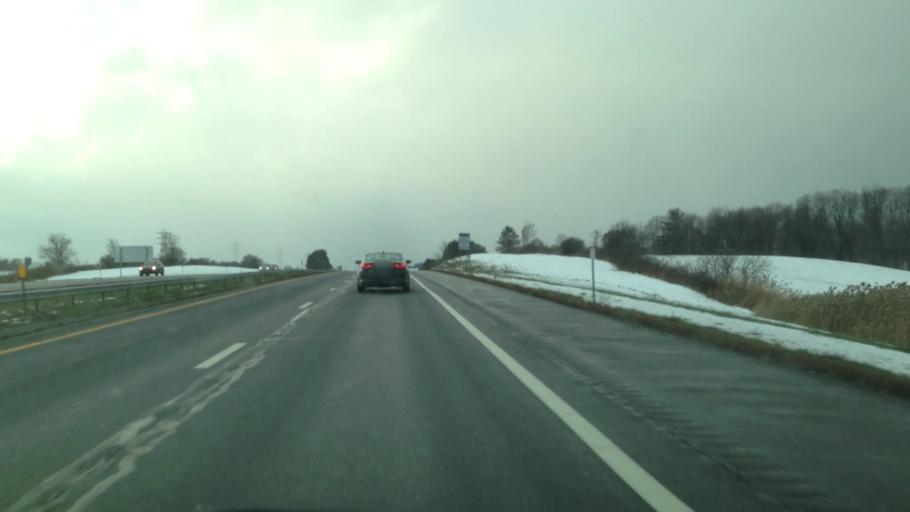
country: US
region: New York
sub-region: Montgomery County
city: Amsterdam
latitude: 42.9302
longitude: -74.2302
